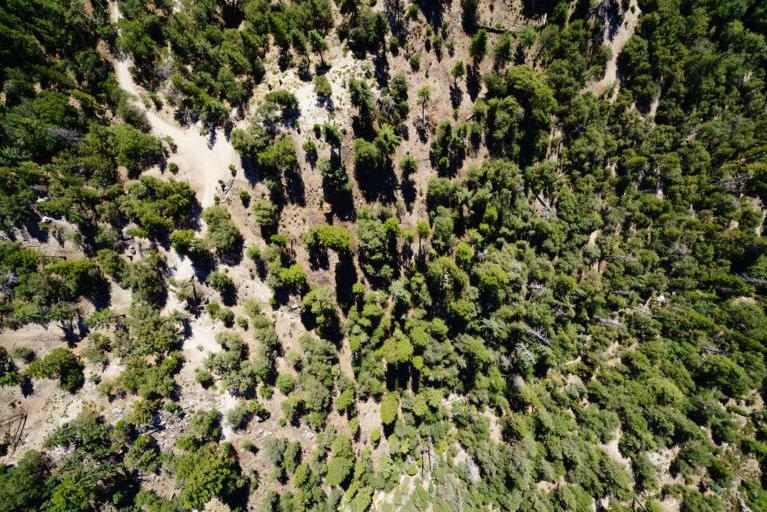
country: US
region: California
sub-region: Riverside County
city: Idyllwild-Pine Cove
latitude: 33.7635
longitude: -116.7447
